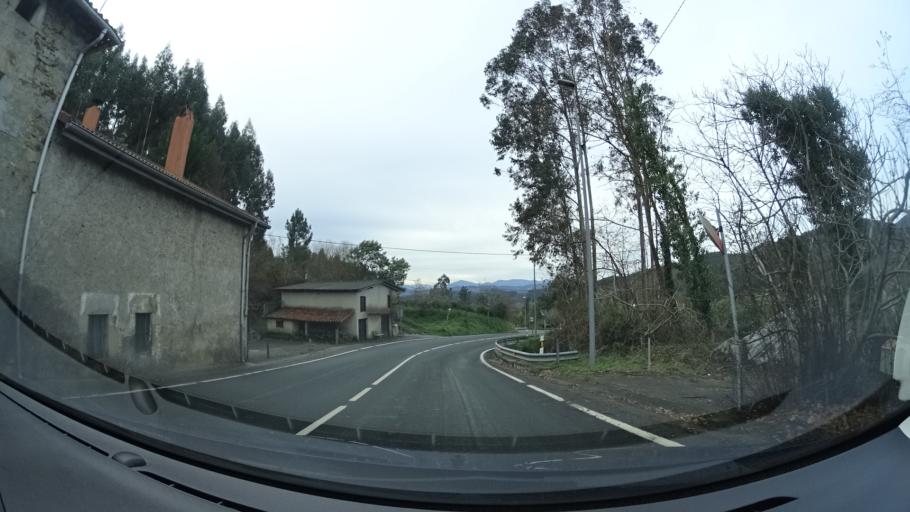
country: ES
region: Basque Country
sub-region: Bizkaia
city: Bakio
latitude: 43.3808
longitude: -2.7900
